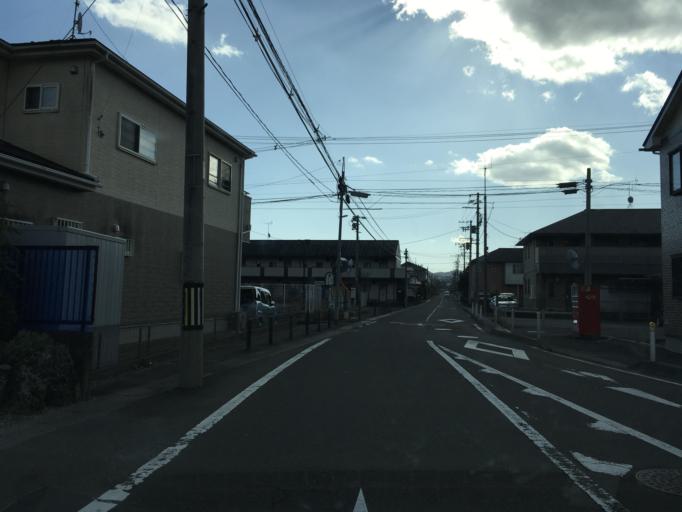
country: JP
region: Miyagi
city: Sendai
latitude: 38.2772
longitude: 140.7644
